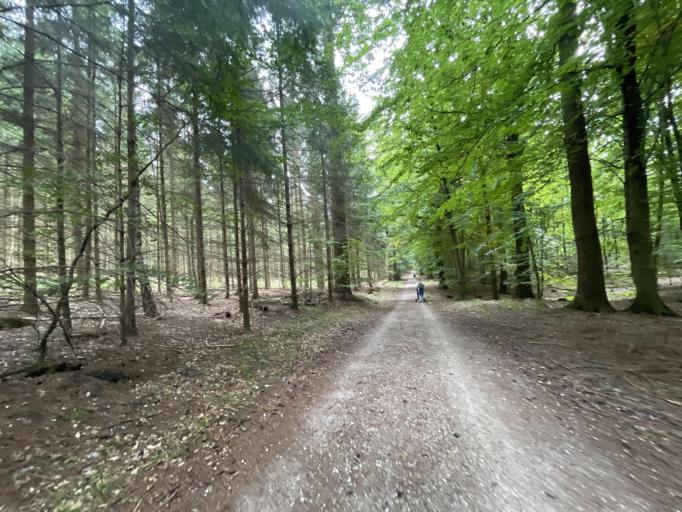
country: DK
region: Capital Region
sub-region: Herlev Kommune
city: Herlev
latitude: 55.7658
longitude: 12.4225
